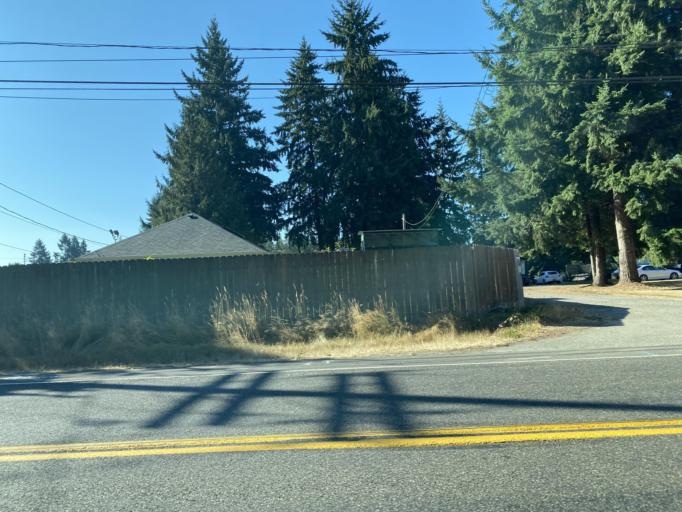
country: US
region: Washington
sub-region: Thurston County
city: Tanglewilde-Thompson Place
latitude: 46.9855
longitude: -122.7417
